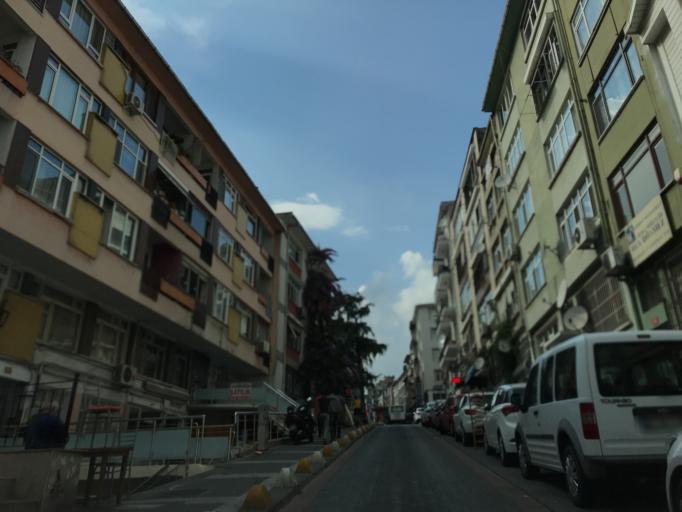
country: TR
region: Istanbul
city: UEskuedar
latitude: 40.9884
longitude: 29.0317
